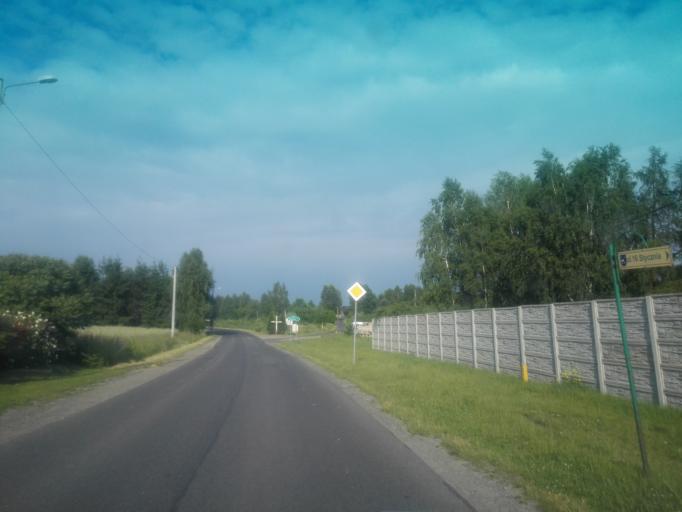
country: PL
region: Silesian Voivodeship
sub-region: Powiat czestochowski
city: Mstow
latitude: 50.8318
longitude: 19.2999
